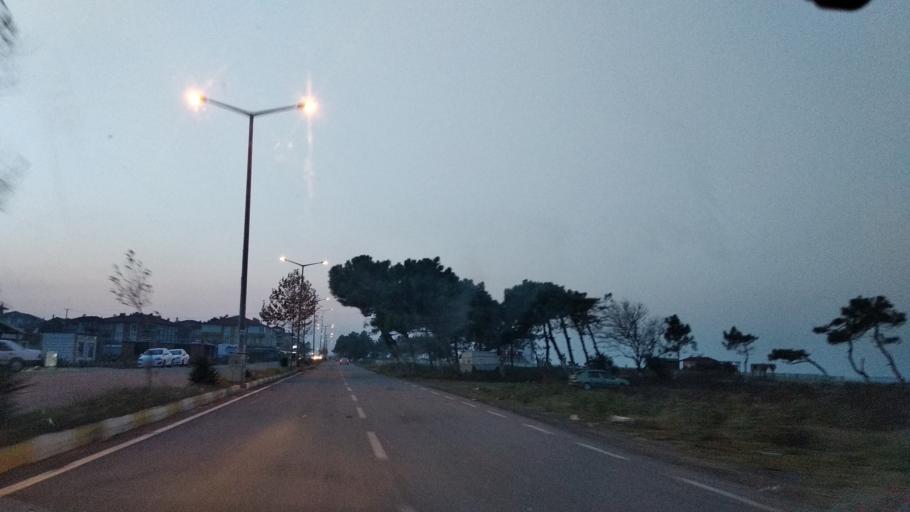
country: TR
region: Sakarya
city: Karasu
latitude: 41.0936
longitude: 30.7360
